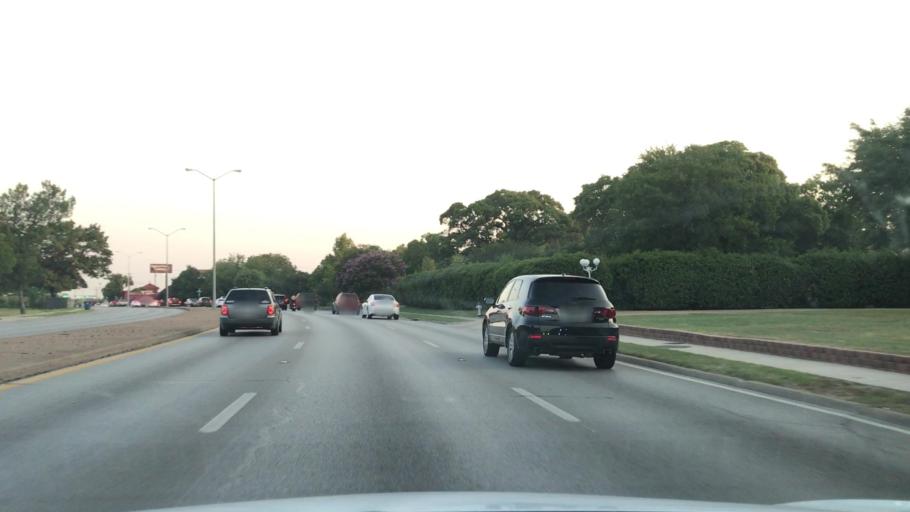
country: US
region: Texas
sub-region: Dallas County
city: Highland Park
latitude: 32.8299
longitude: -96.6981
